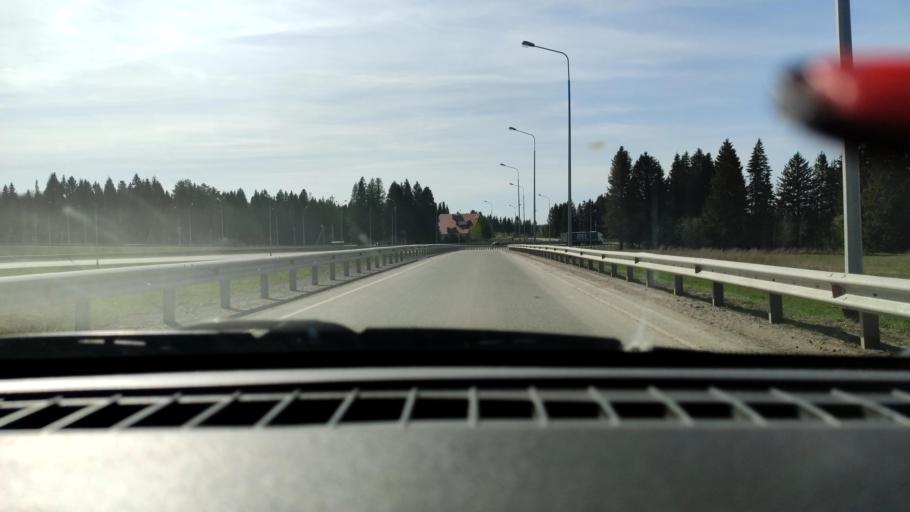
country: RU
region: Perm
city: Kukushtan
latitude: 57.6362
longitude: 56.4569
